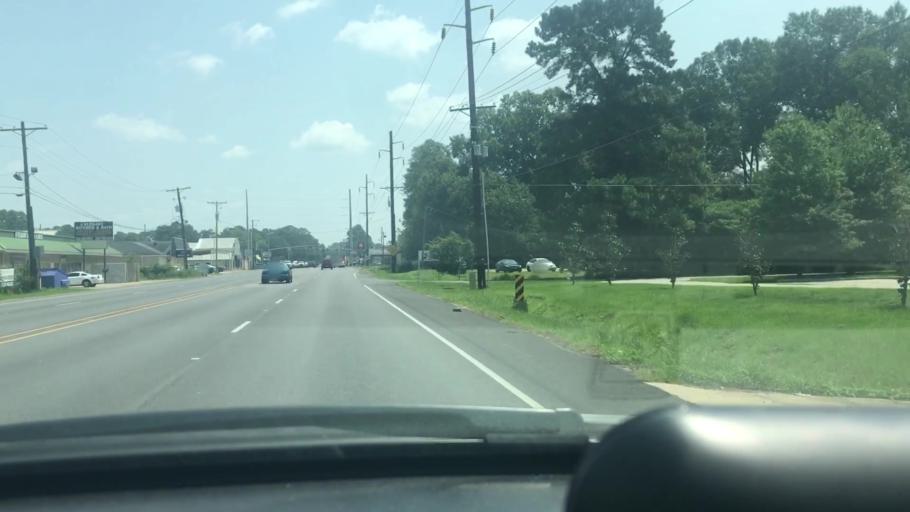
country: US
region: Louisiana
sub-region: Livingston Parish
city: Denham Springs
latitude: 30.4844
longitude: -90.9464
